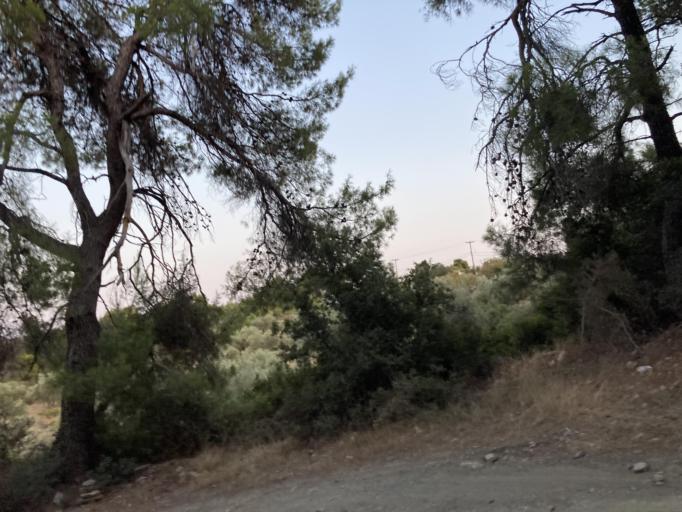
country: GR
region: Thessaly
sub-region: Nomos Magnisias
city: Patitirion
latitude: 39.1528
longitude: 23.8761
